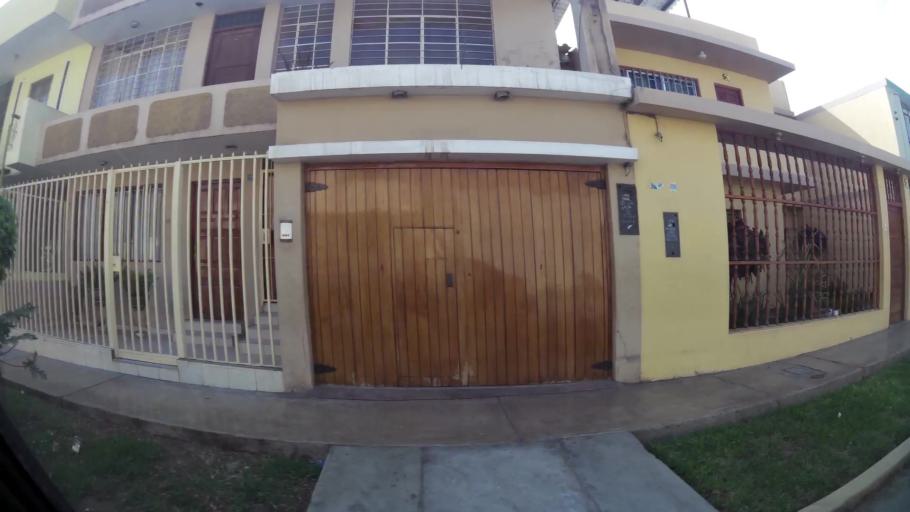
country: PE
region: La Libertad
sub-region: Provincia de Trujillo
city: Trujillo
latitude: -8.1086
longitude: -79.0148
